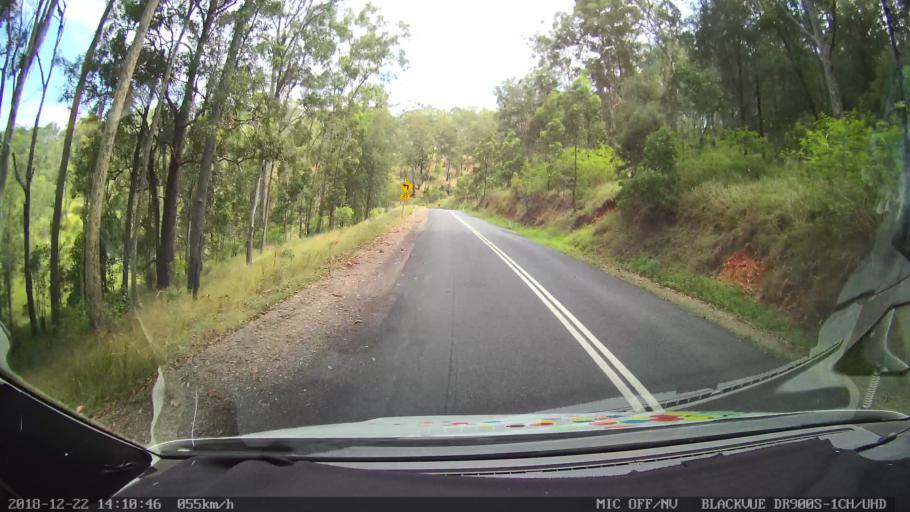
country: AU
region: New South Wales
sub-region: Clarence Valley
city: Coutts Crossing
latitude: -29.9950
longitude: 152.7091
